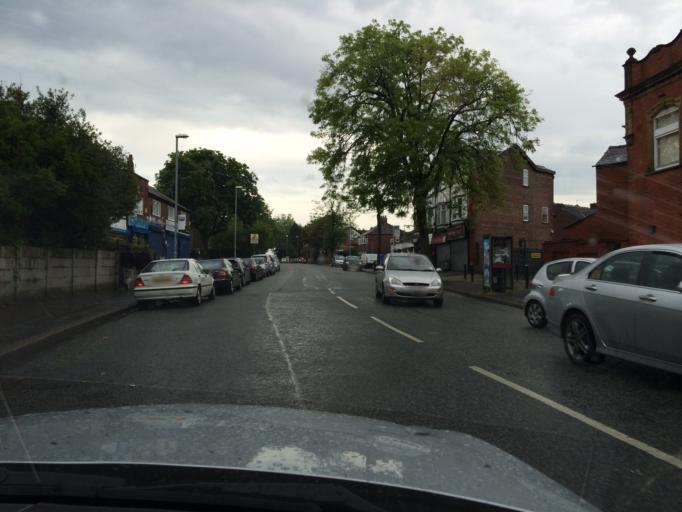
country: GB
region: England
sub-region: Manchester
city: Burnage
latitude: 53.4432
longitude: -2.1991
